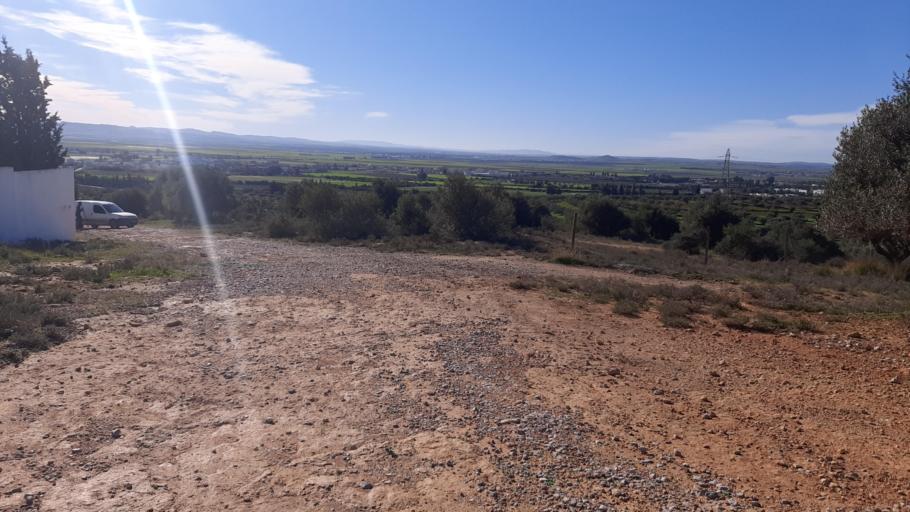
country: TN
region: Tunis
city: Oued Lill
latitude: 36.7664
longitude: 9.9857
